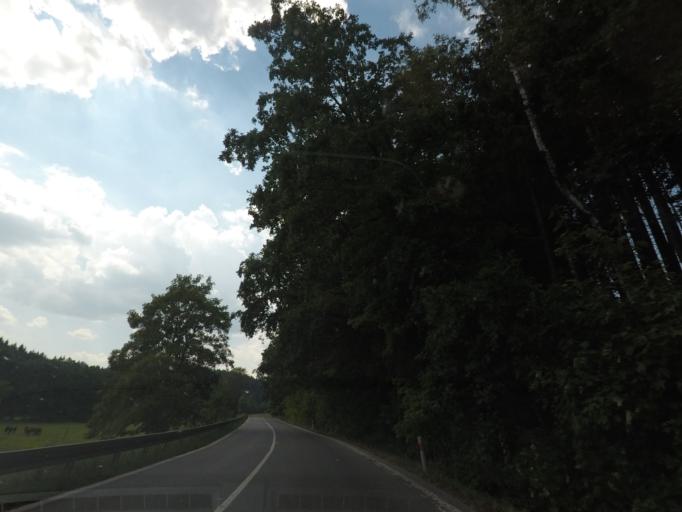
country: CZ
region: Kralovehradecky
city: Pilnikov
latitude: 50.5531
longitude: 15.8463
